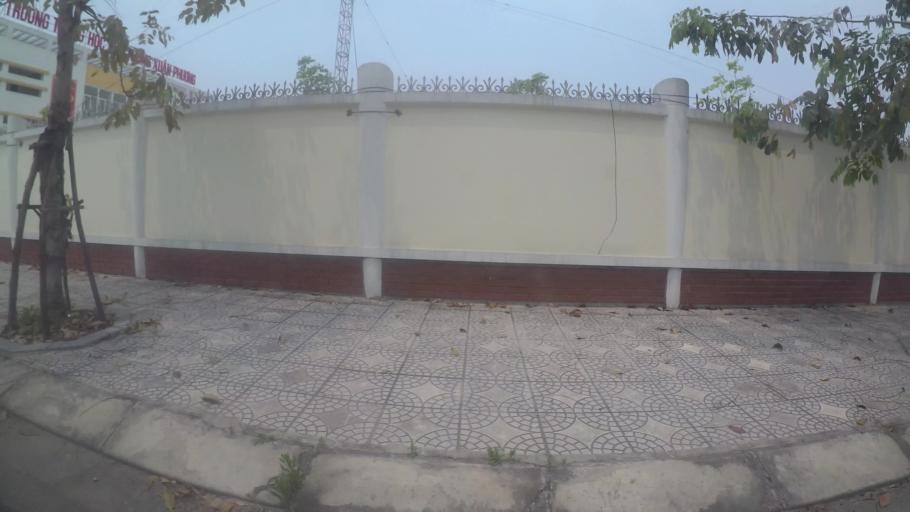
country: VN
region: Ha Noi
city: Cau Dien
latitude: 21.0315
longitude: 105.7476
